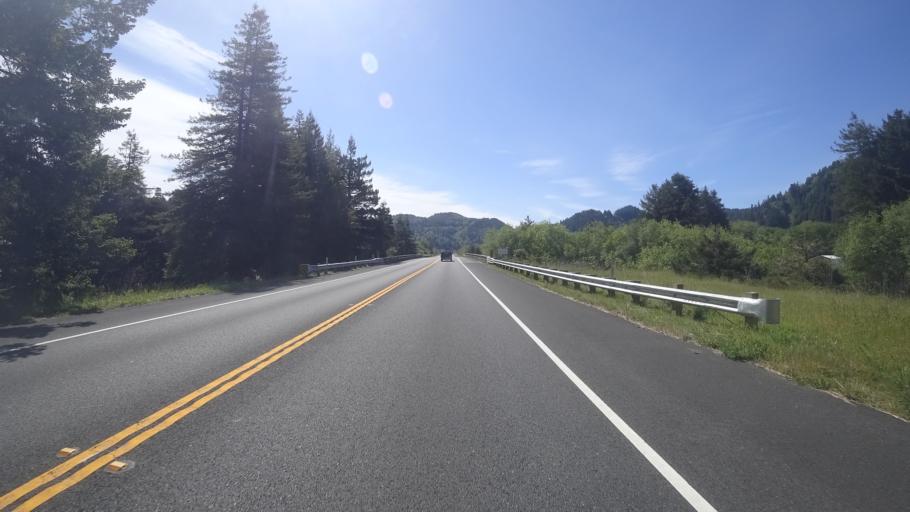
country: US
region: California
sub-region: Del Norte County
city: Bertsch-Oceanview
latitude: 41.5240
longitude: -124.0347
